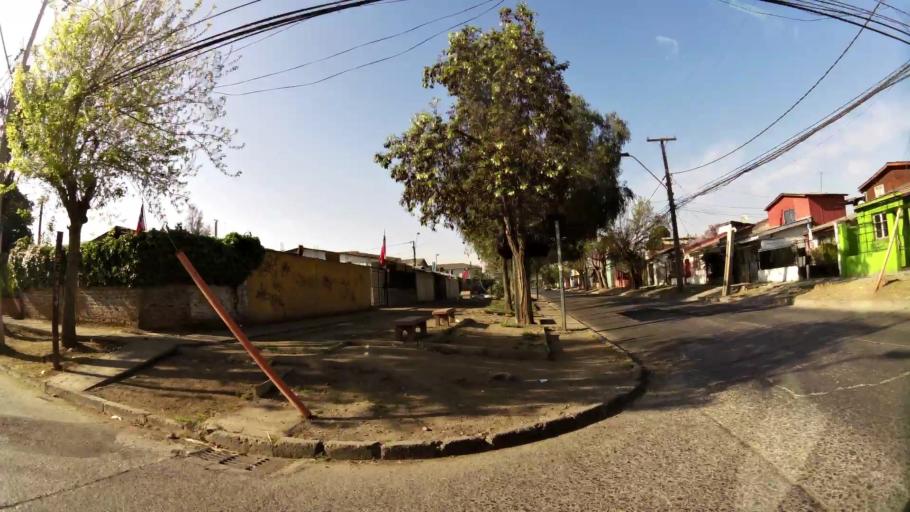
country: CL
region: Santiago Metropolitan
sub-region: Provincia de Santiago
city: Santiago
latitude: -33.3901
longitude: -70.6688
